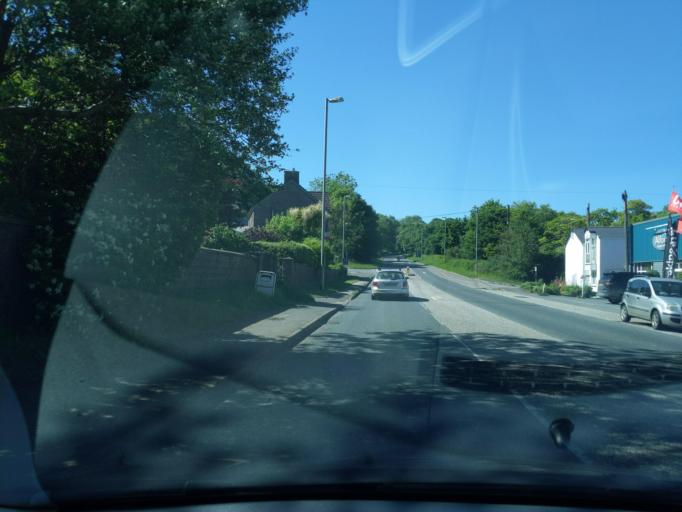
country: GB
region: England
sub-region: Cornwall
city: Helston
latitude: 50.1013
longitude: -5.2810
